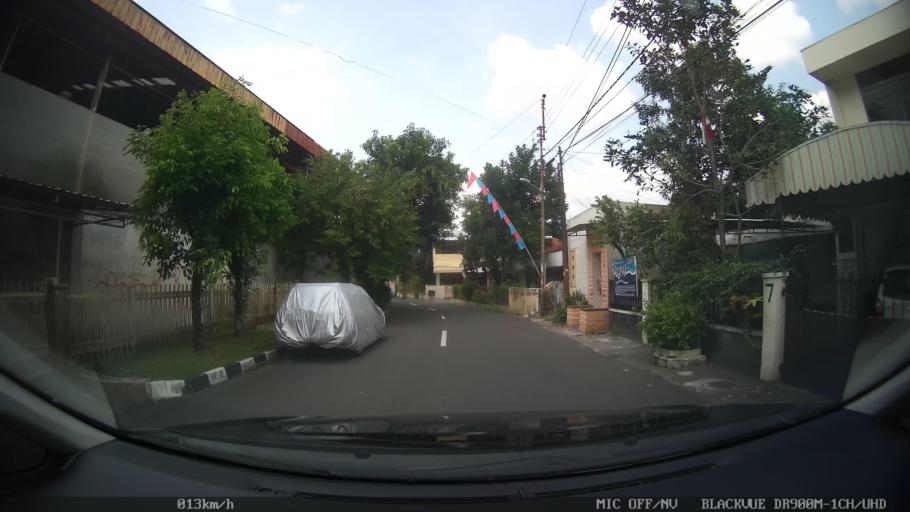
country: ID
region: Daerah Istimewa Yogyakarta
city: Yogyakarta
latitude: -7.7853
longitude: 110.3822
